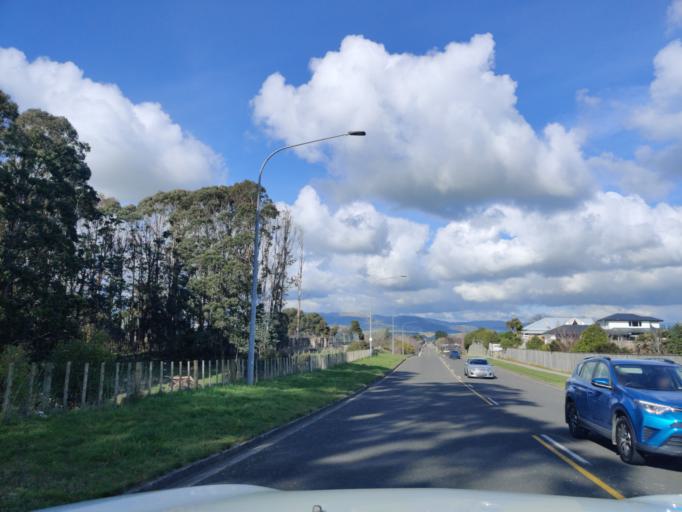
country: NZ
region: Manawatu-Wanganui
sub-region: Palmerston North City
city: Palmerston North
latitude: -40.3220
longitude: 175.6594
